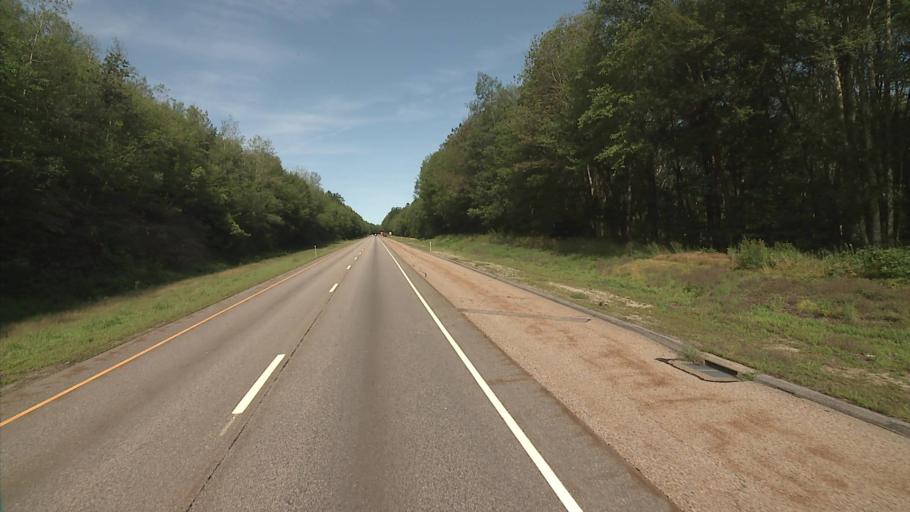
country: US
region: Connecticut
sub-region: New London County
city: Colchester
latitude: 41.5692
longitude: -72.2745
